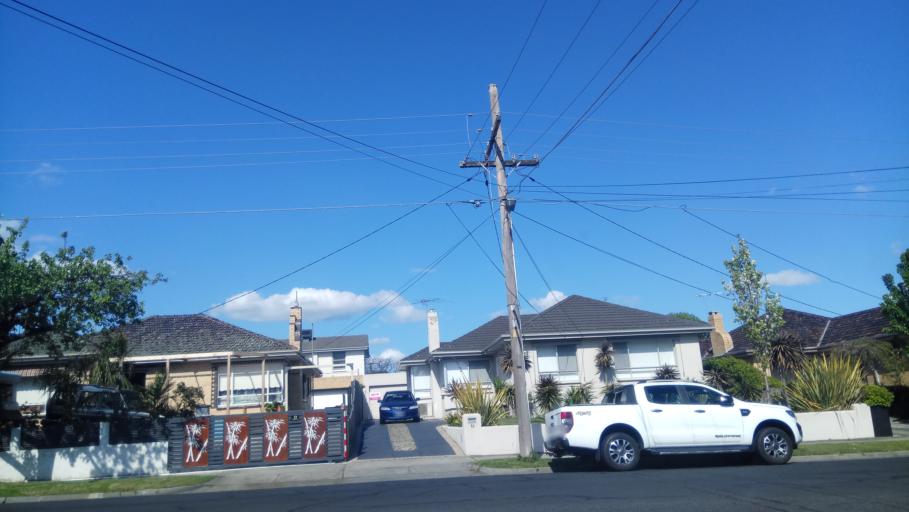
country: AU
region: Victoria
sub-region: Kingston
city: Dingley Village
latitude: -37.9844
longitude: 145.1312
